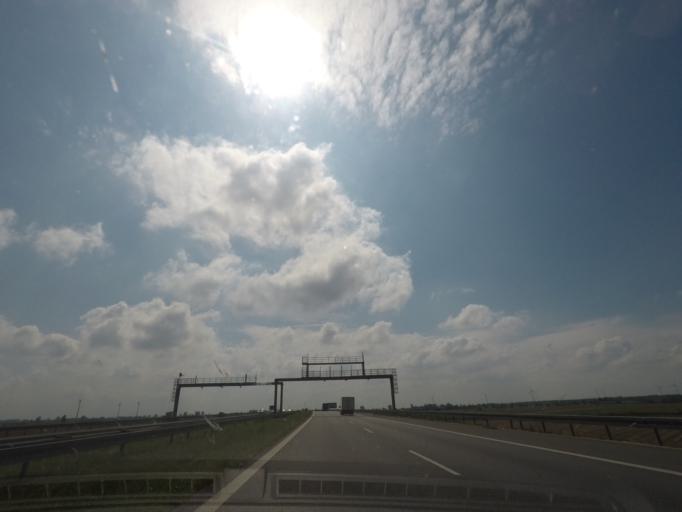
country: PL
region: Lodz Voivodeship
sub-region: Powiat kutnowski
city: Krzyzanow
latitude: 52.2330
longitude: 19.4559
